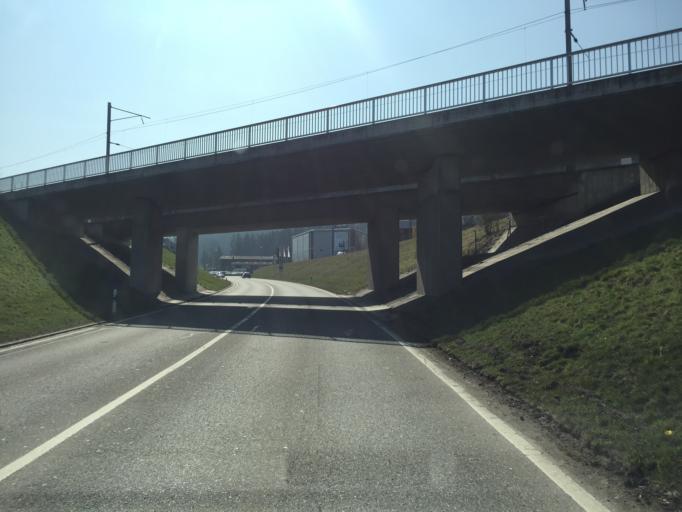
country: CH
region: Saint Gallen
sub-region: Wahlkreis Wil
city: Wil
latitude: 47.4425
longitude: 9.0540
